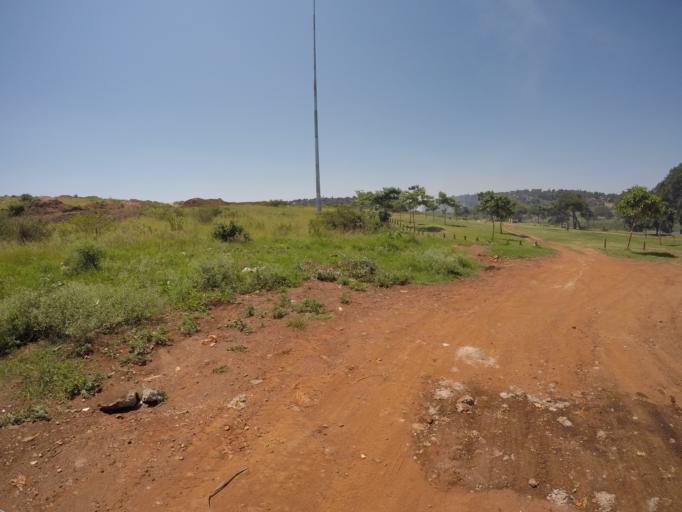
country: ZA
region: KwaZulu-Natal
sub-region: uThungulu District Municipality
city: Empangeni
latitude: -28.7707
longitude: 31.8831
